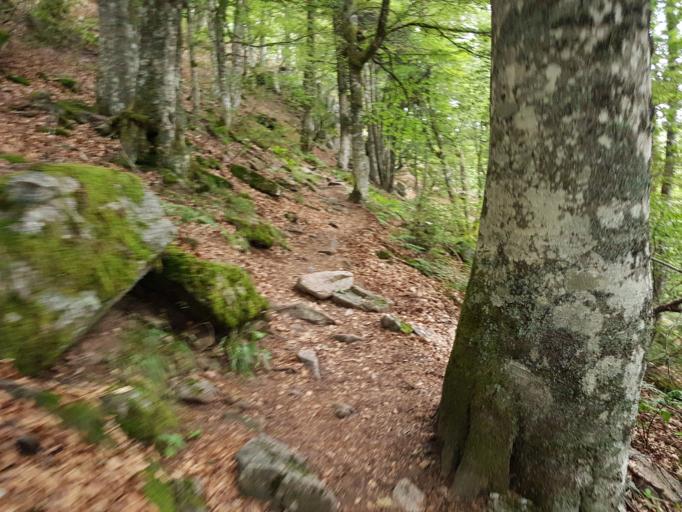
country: FR
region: Alsace
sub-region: Departement du Haut-Rhin
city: Soultzeren
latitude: 48.0907
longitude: 7.0599
